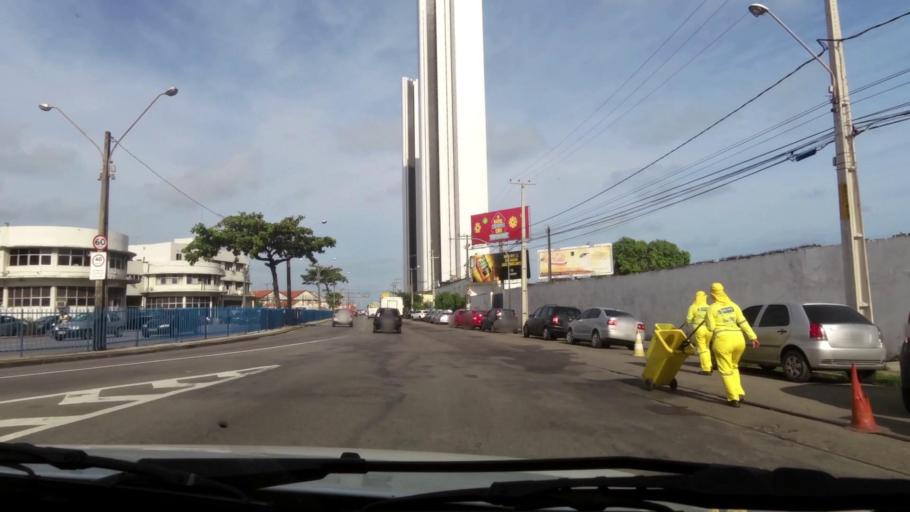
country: BR
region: Pernambuco
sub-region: Recife
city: Recife
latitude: -8.0712
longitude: -34.8763
